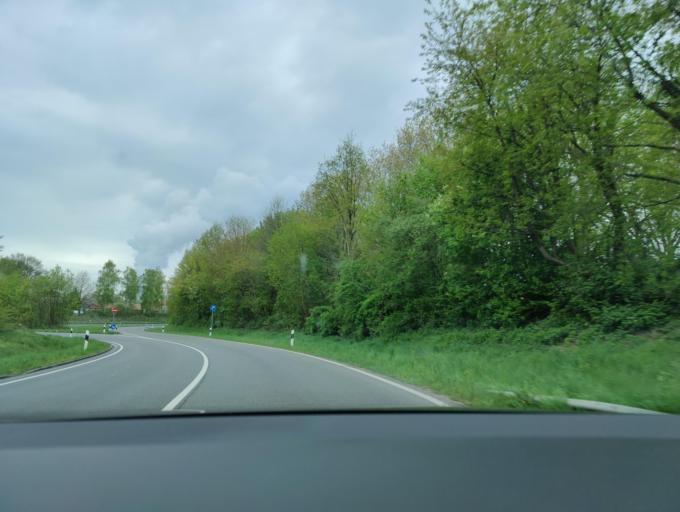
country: DE
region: Lower Saxony
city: Lingen
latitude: 52.4950
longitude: 7.3282
